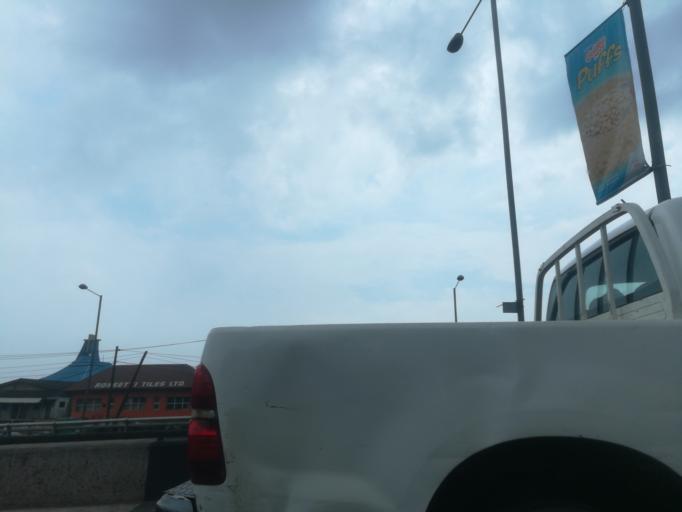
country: NG
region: Lagos
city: Surulere
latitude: 6.4880
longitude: 3.3640
